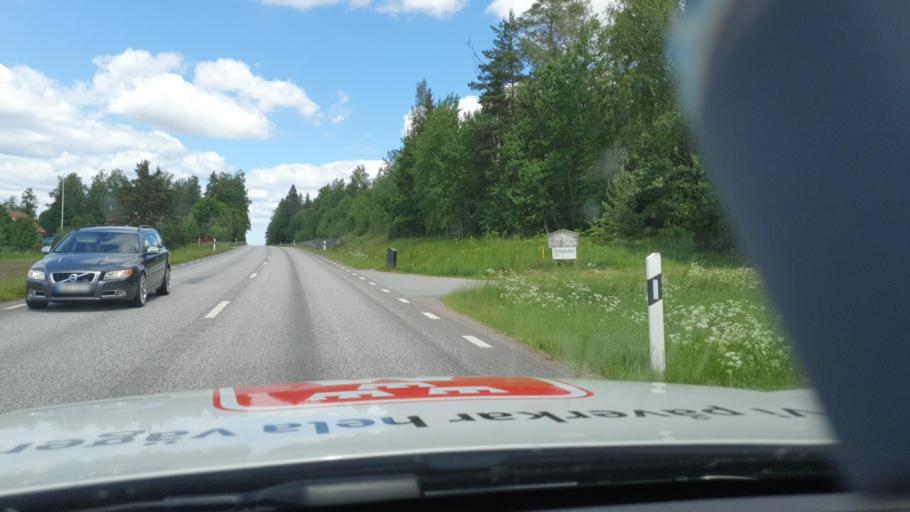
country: SE
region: Uppsala
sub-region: Uppsala Kommun
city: Vattholma
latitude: 60.0633
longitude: 17.7563
